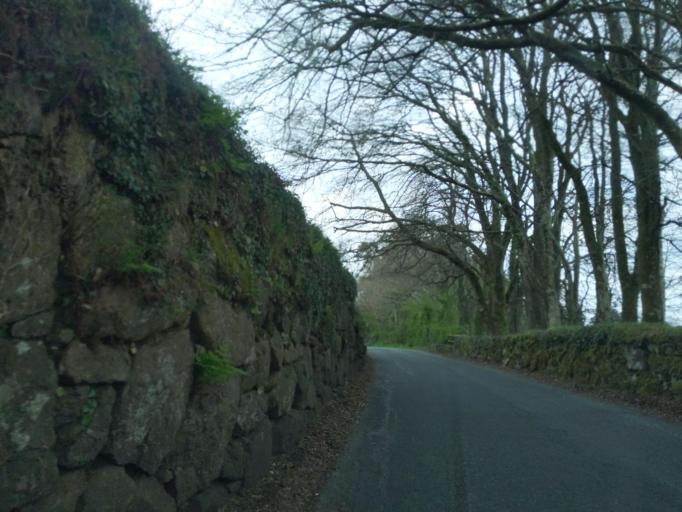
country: GB
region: England
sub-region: Devon
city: Bovey Tracey
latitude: 50.6507
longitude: -3.8064
